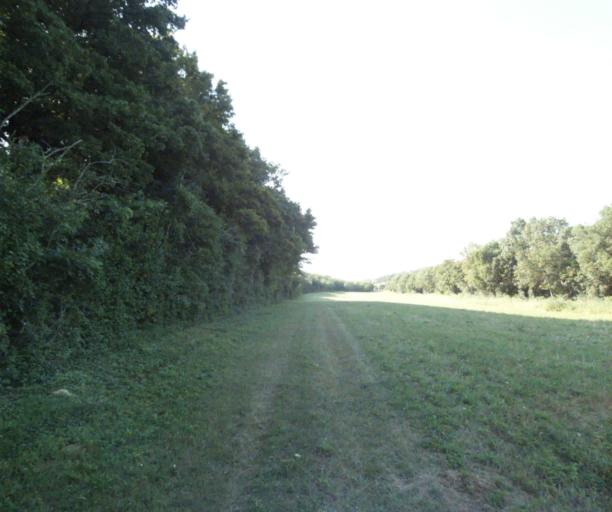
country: FR
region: Midi-Pyrenees
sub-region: Departement de la Haute-Garonne
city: Saint-Felix-Lauragais
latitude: 43.4353
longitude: 1.8226
